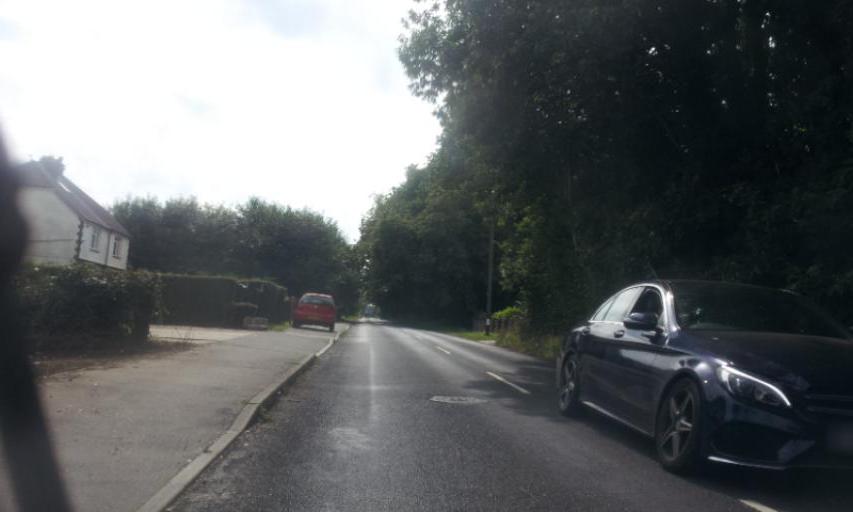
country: GB
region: England
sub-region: Kent
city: Wateringbury
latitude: 51.2740
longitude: 0.4331
